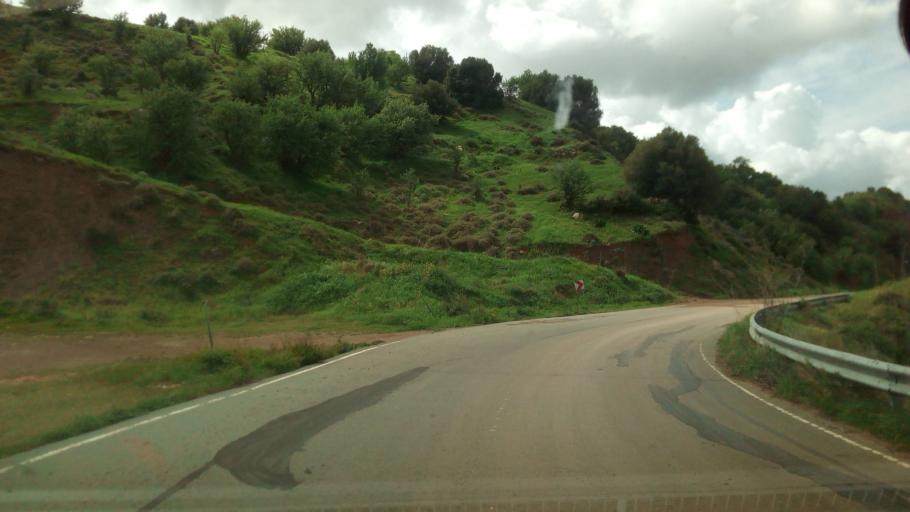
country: CY
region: Pafos
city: Mesogi
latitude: 34.8736
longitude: 32.5858
